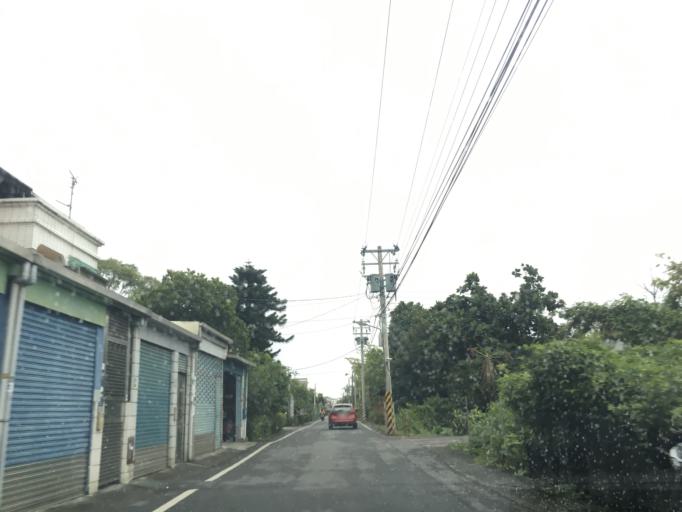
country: TW
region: Taiwan
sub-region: Hualien
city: Hualian
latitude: 23.9904
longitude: 121.5710
